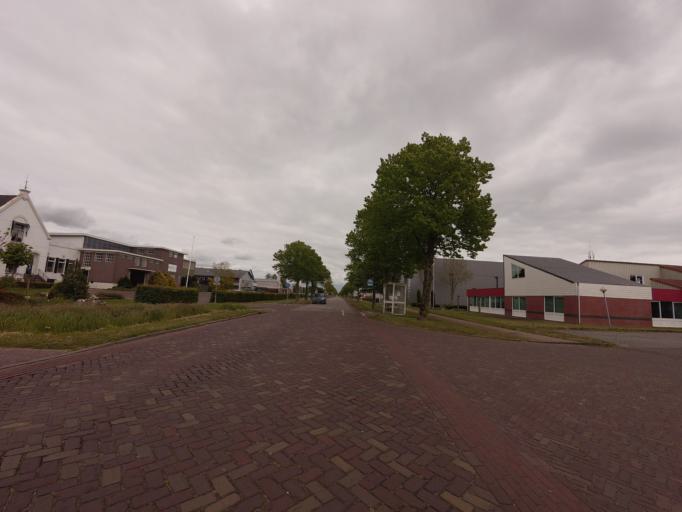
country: NL
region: Friesland
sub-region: Sudwest Fryslan
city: Woudsend
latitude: 52.9431
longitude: 5.6334
